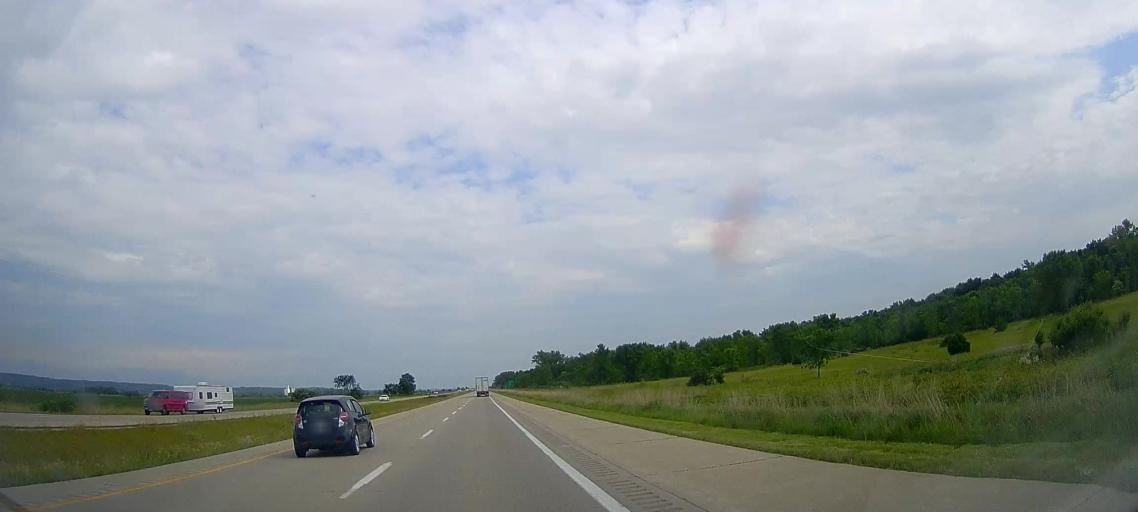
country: US
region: Nebraska
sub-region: Burt County
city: Tekamah
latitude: 41.8191
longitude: -96.0715
